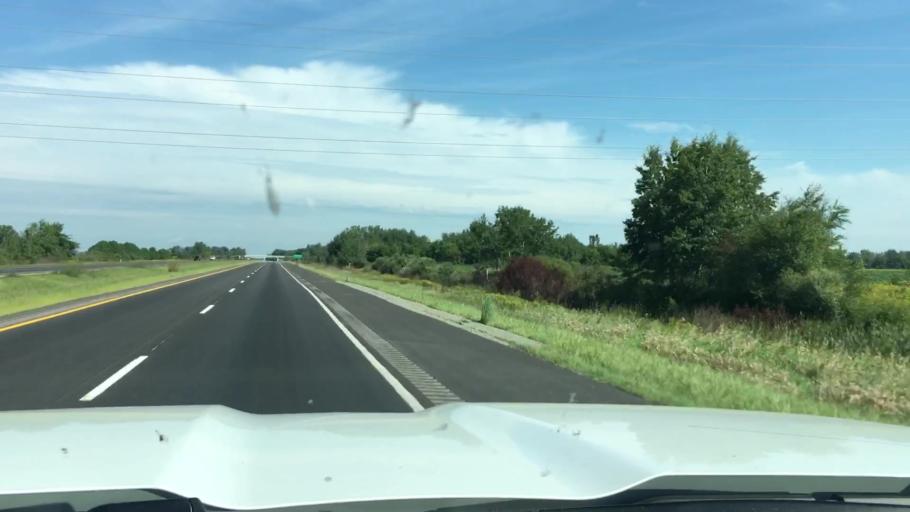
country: US
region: Michigan
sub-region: Saginaw County
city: Freeland
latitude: 43.5561
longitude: -84.1384
